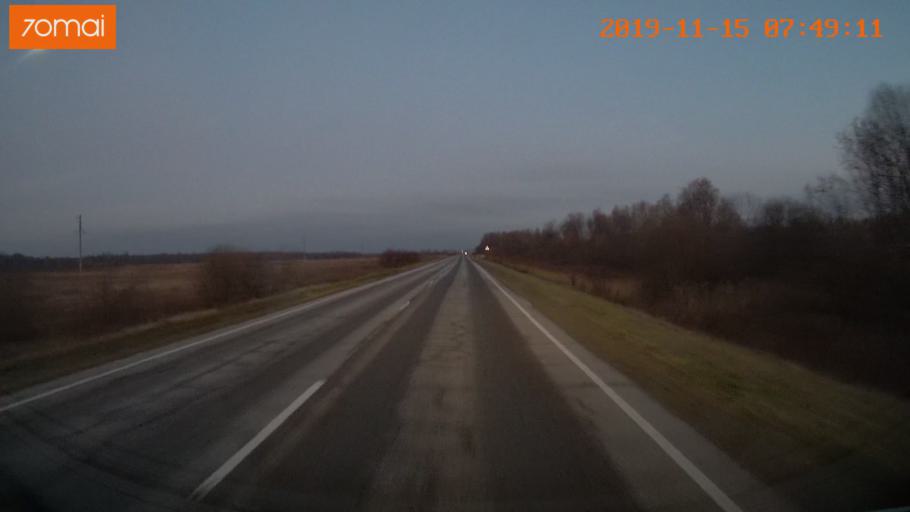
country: RU
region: Vologda
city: Cherepovets
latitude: 58.8585
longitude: 38.2335
